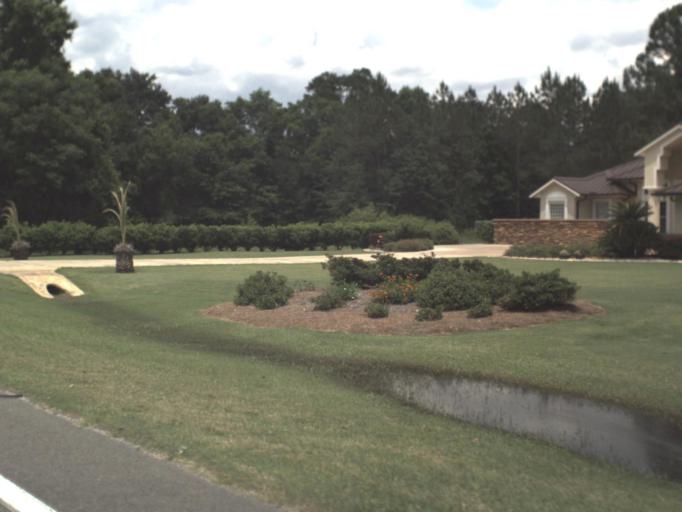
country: US
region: Florida
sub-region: Columbia County
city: Five Points
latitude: 30.3111
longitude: -82.6305
